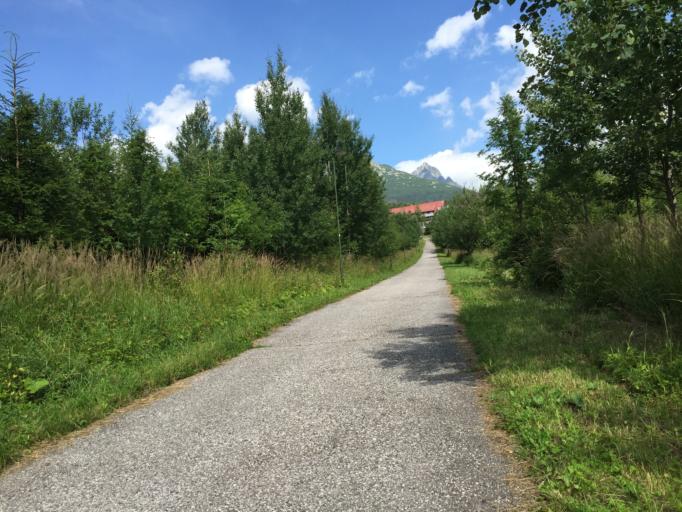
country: SK
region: Presovsky
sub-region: Okres Poprad
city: Vysoke Tatry
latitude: 49.1374
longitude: 20.2368
